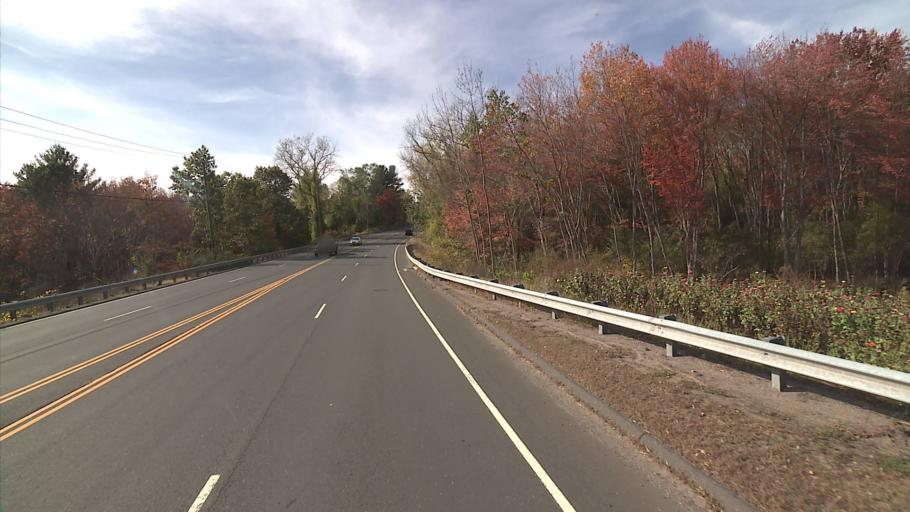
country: US
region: Connecticut
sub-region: Hartford County
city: Plainville
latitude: 41.7047
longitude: -72.8651
